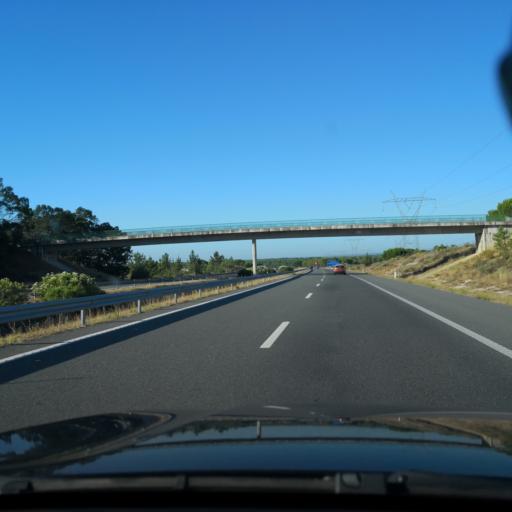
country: PT
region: Setubal
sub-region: Grandola
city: Grandola
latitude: 38.2553
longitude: -8.5215
